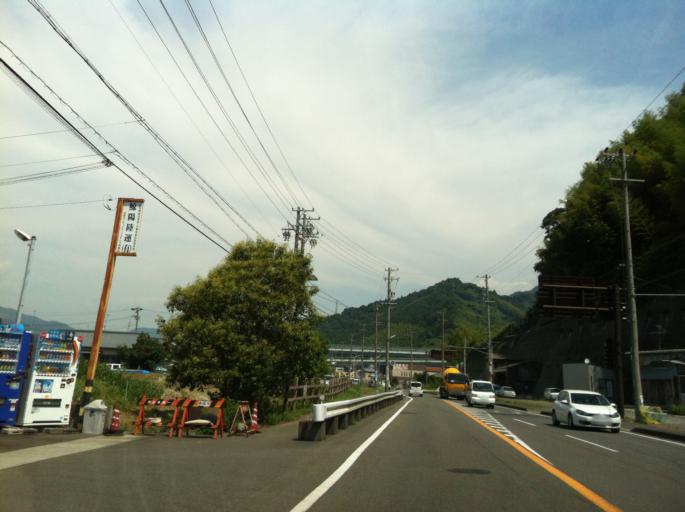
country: JP
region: Shizuoka
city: Shizuoka-shi
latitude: 35.0362
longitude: 138.3799
